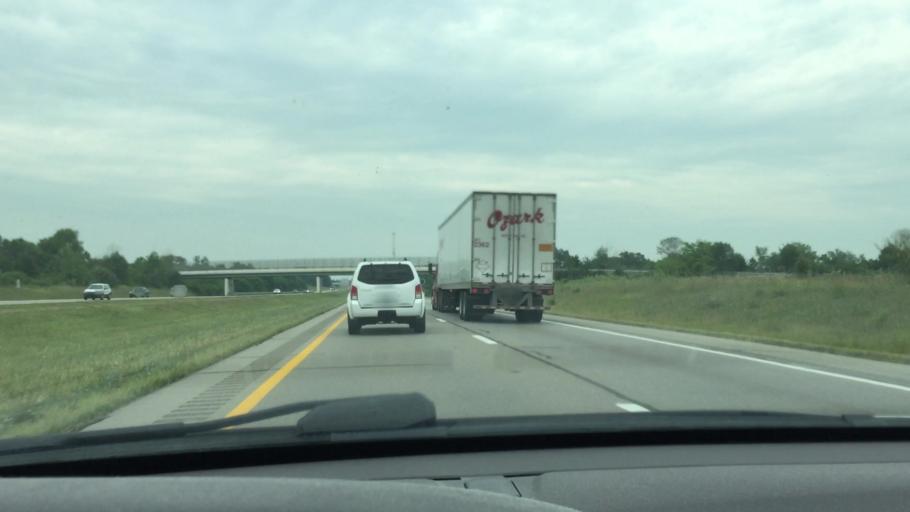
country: US
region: Ohio
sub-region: Clinton County
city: Wilmington
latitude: 39.4965
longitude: -83.9099
